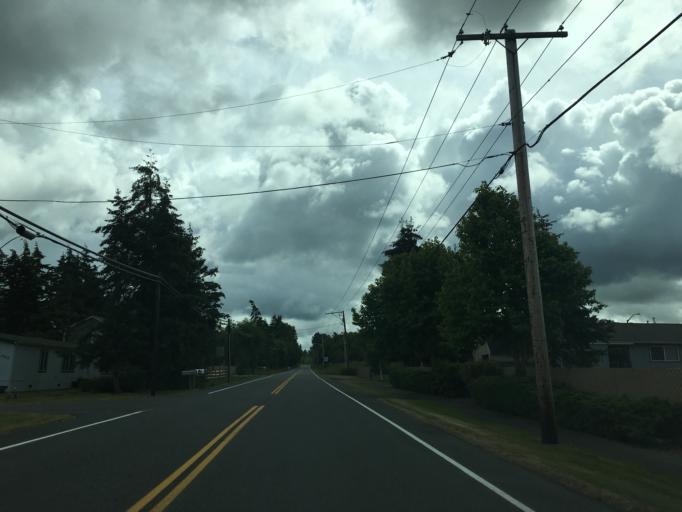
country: US
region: Washington
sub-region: Whatcom County
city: Birch Bay
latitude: 48.9177
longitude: -122.7369
